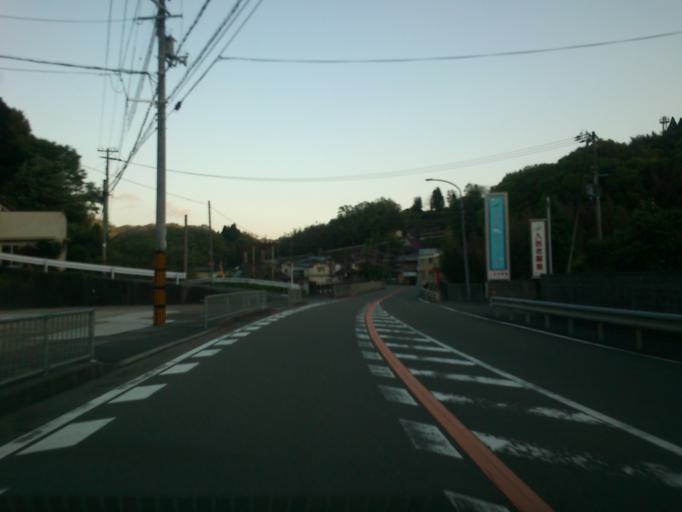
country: JP
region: Kyoto
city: Ayabe
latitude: 35.2134
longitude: 135.4248
